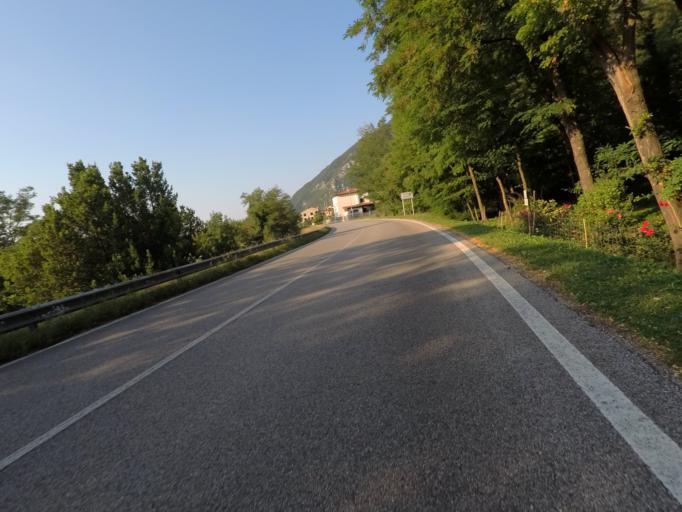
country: IT
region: Friuli Venezia Giulia
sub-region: Provincia di Udine
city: Trasaghis
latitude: 46.2618
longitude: 13.0410
